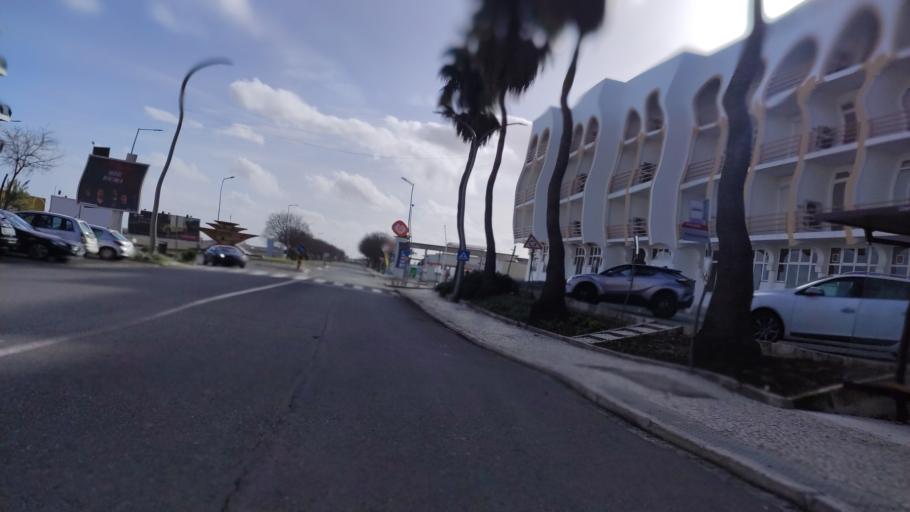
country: PT
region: Beja
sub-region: Beja
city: Beja
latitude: 38.0063
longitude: -7.8654
